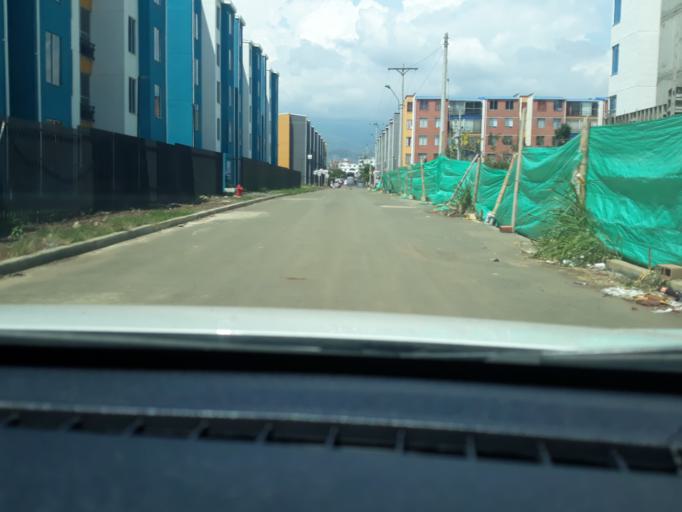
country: CO
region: Valle del Cauca
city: Cali
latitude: 3.3831
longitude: -76.5089
